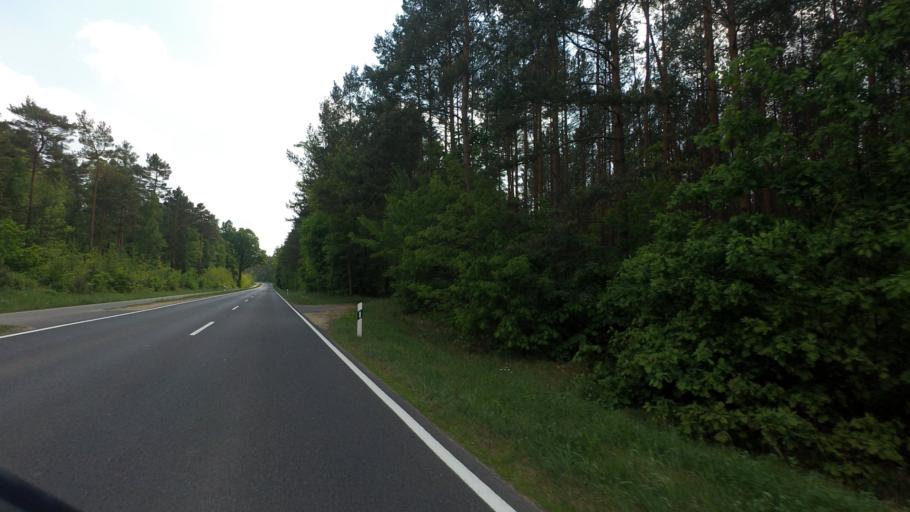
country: DE
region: Saxony
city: Niesky
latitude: 51.3120
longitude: 14.8259
